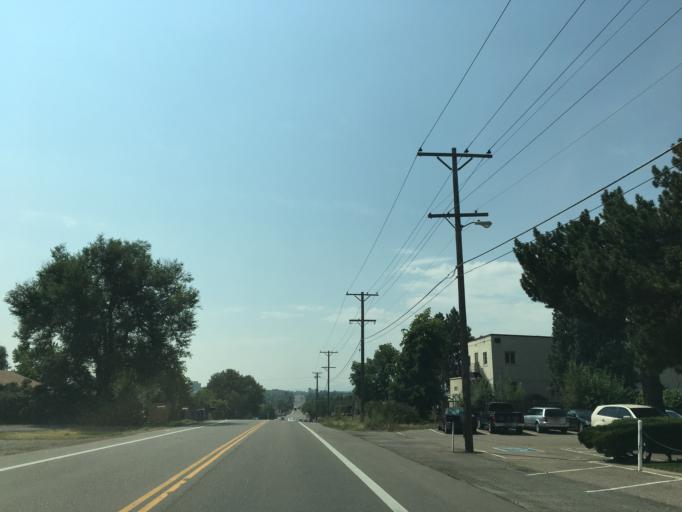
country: US
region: Colorado
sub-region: Jefferson County
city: Applewood
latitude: 39.7433
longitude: -105.1283
